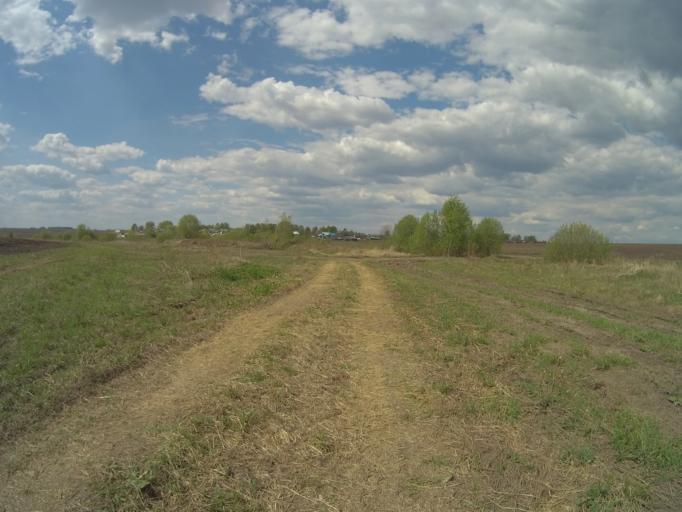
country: RU
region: Vladimir
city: Suzdal'
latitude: 56.3381
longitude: 40.3428
